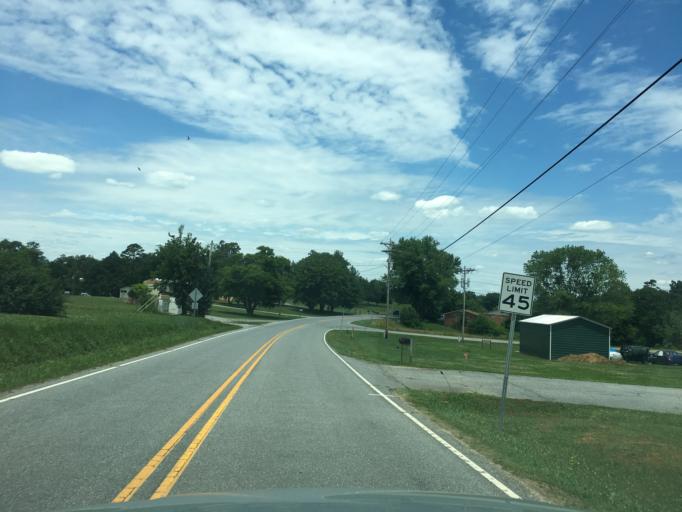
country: US
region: North Carolina
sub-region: Burke County
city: Glen Alpine
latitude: 35.6777
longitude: -81.7684
